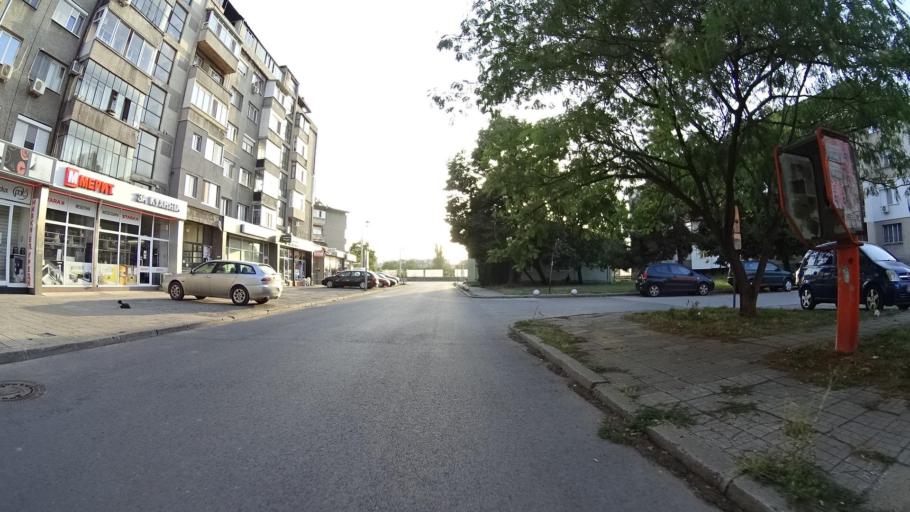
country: BG
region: Plovdiv
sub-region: Obshtina Plovdiv
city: Plovdiv
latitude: 42.1318
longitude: 24.7459
